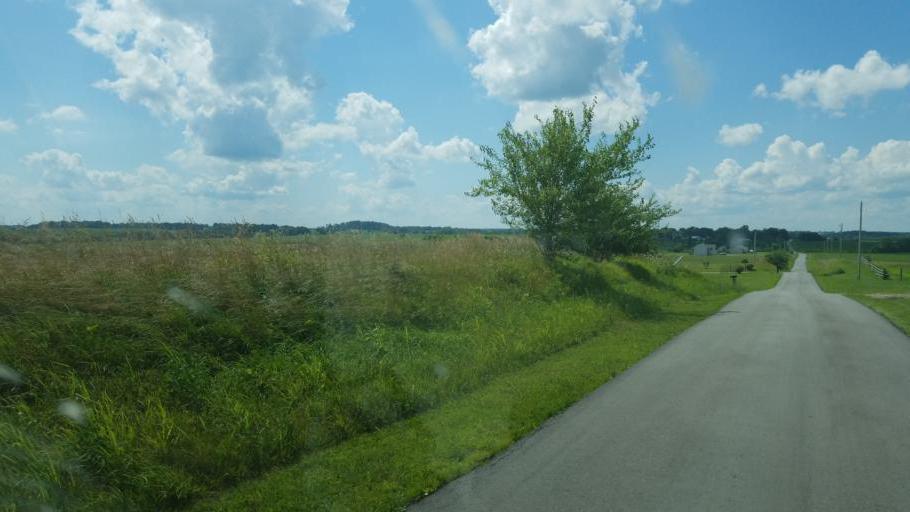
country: US
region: Ohio
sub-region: Highland County
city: Greenfield
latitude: 39.2550
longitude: -83.4308
